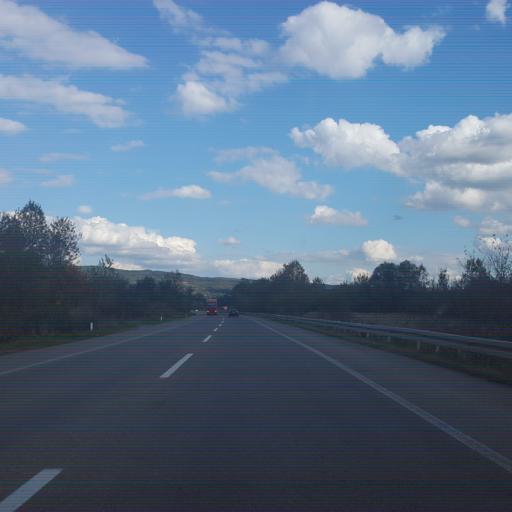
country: RS
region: Central Serbia
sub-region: Rasinski Okrug
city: Krusevac
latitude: 43.6093
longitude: 21.3330
